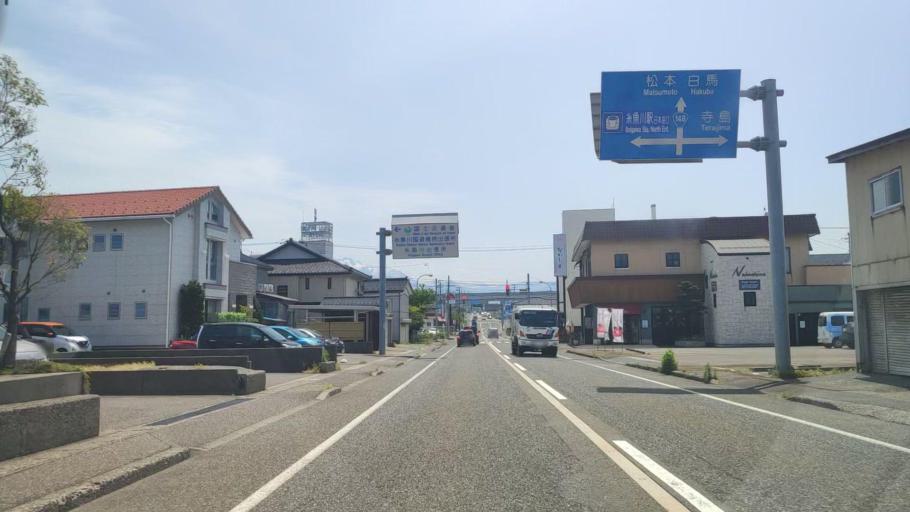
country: JP
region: Niigata
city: Itoigawa
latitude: 37.0442
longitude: 137.8507
